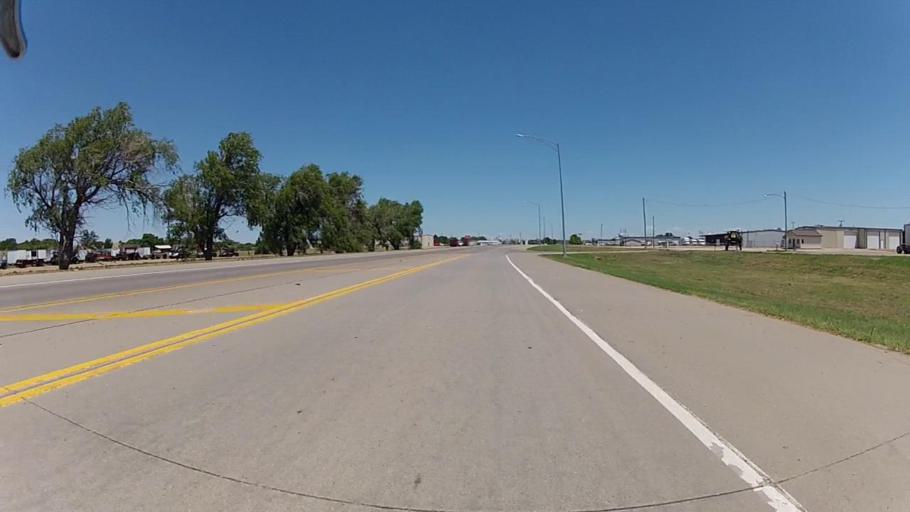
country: US
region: Kansas
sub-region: Ford County
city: Dodge City
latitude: 37.7308
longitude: -100.0190
